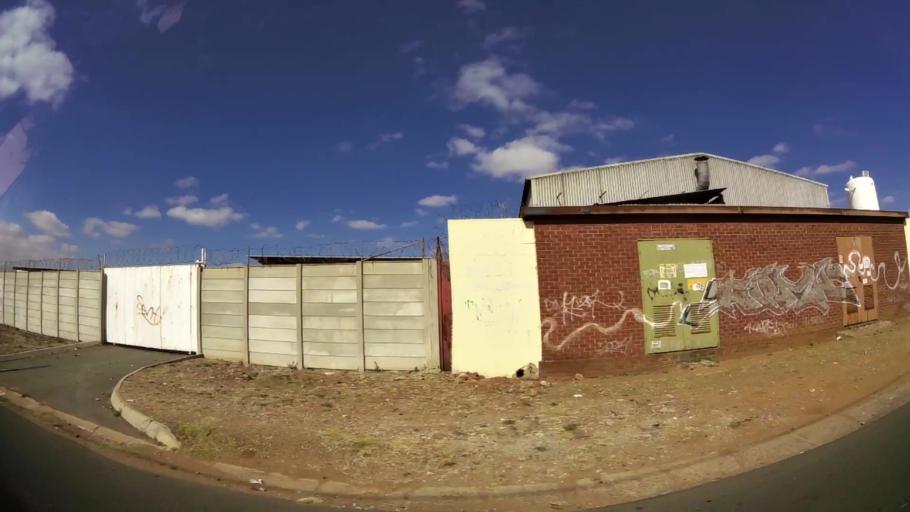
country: ZA
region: Gauteng
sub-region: West Rand District Municipality
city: Krugersdorp
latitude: -26.1168
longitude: 27.8144
